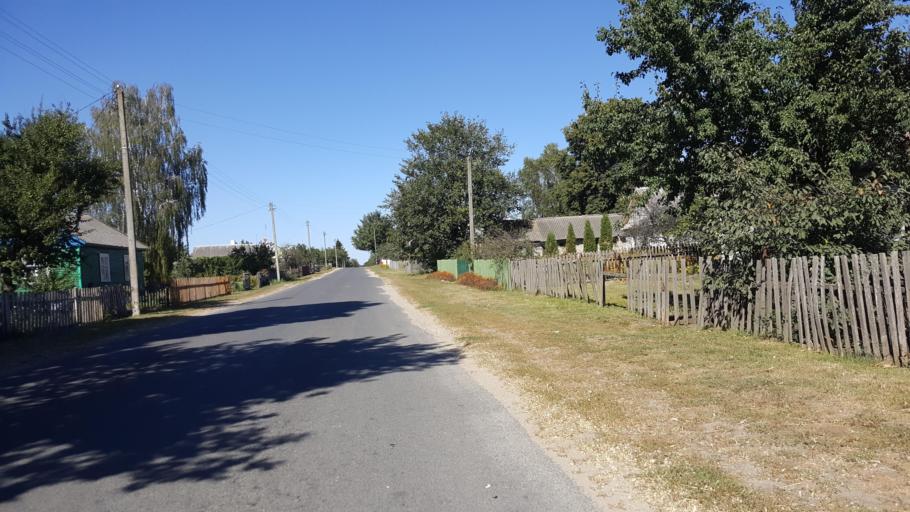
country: PL
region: Lublin Voivodeship
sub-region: Powiat bialski
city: Rokitno
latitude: 52.2352
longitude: 23.3413
